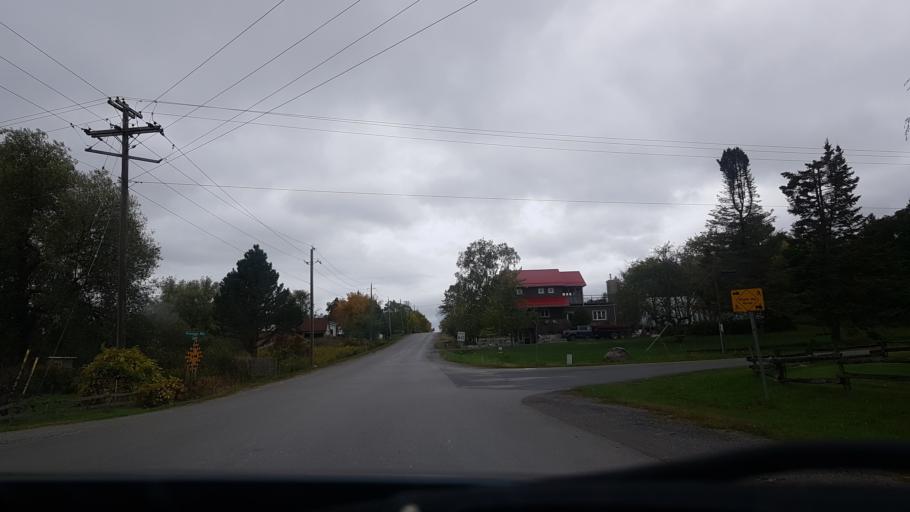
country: CA
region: Ontario
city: Peterborough
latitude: 44.2538
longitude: -78.4083
